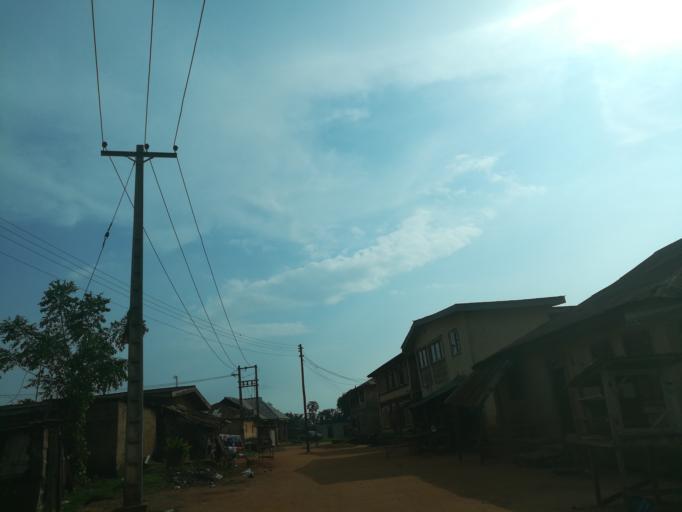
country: NG
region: Lagos
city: Ikorodu
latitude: 6.6627
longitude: 3.6701
